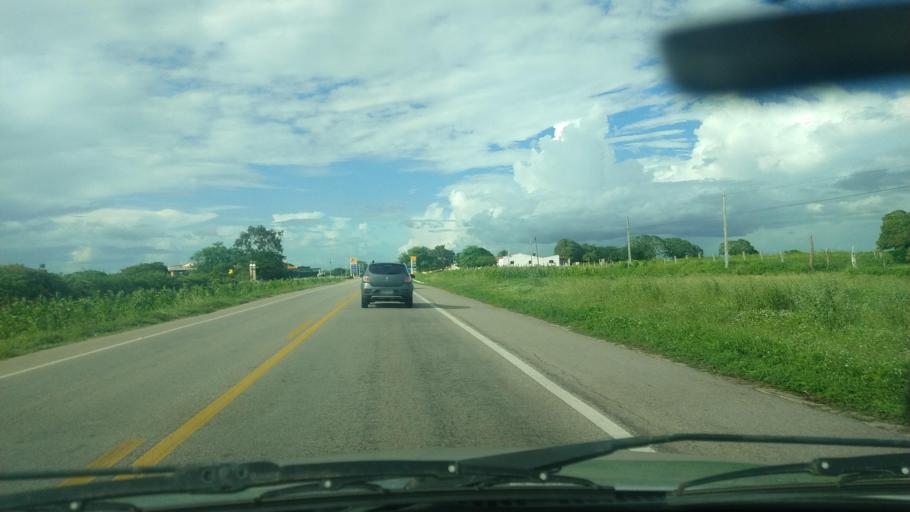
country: BR
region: Rio Grande do Norte
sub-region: Tangara
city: Tangara
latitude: -6.1756
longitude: -35.7667
